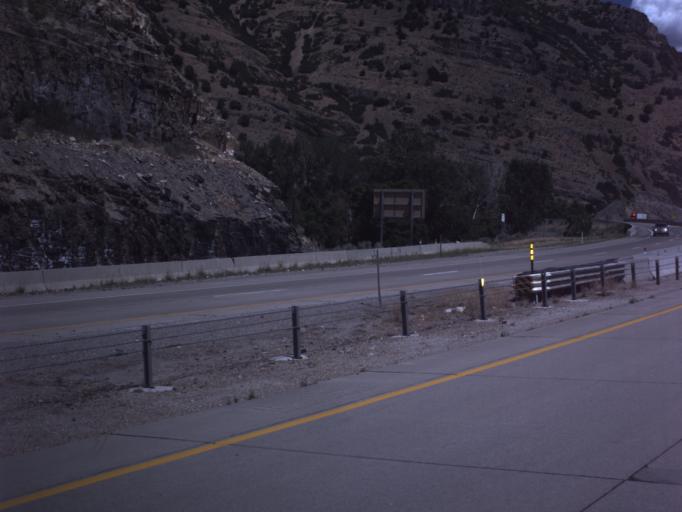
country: US
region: Utah
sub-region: Morgan County
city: Morgan
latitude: 41.0494
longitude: -111.6055
